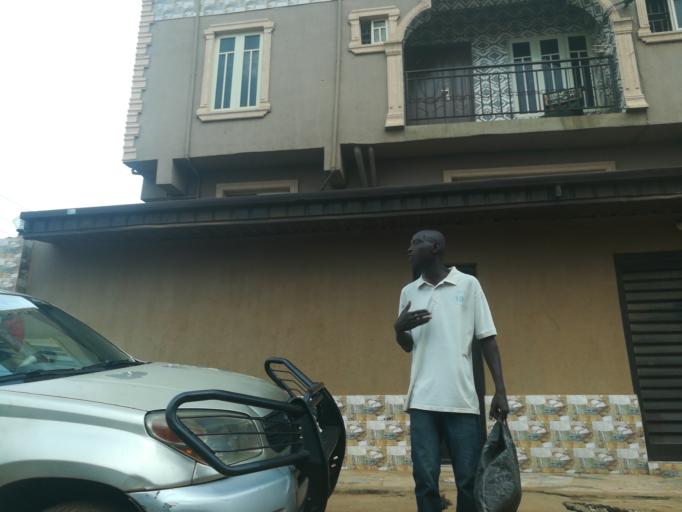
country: NG
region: Lagos
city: Ikorodu
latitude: 6.6244
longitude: 3.4979
